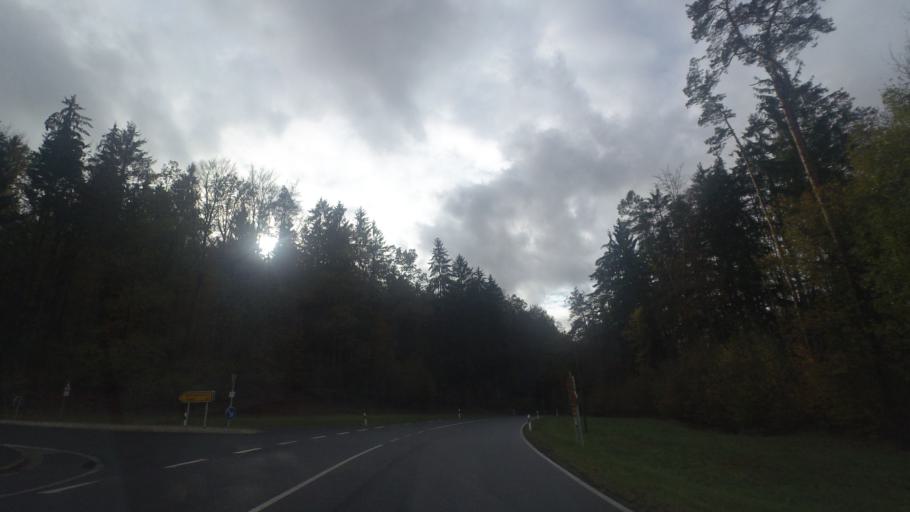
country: DE
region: Bavaria
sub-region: Regierungsbezirk Unterfranken
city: Aubstadt
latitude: 50.3444
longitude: 10.4131
